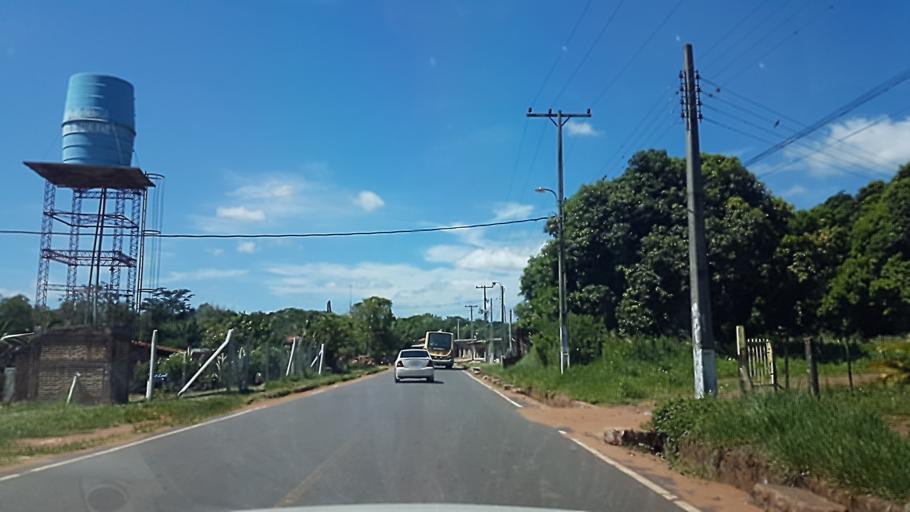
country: PY
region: Central
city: Capiata
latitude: -25.3338
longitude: -57.4341
